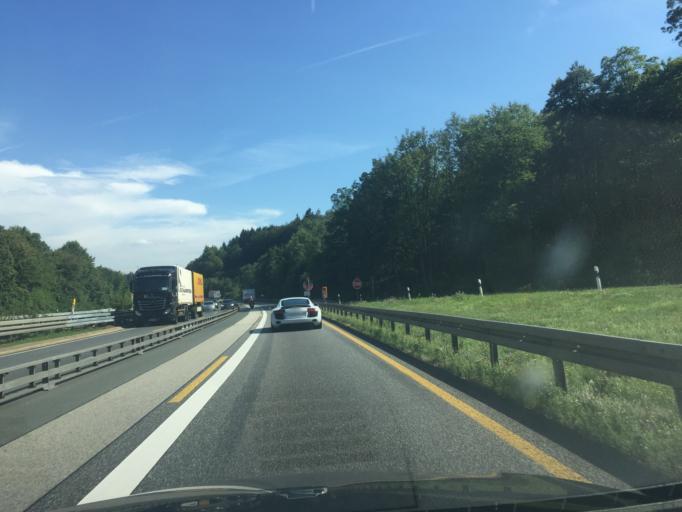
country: DE
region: Hesse
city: Dillenburg
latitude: 50.7247
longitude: 8.2811
